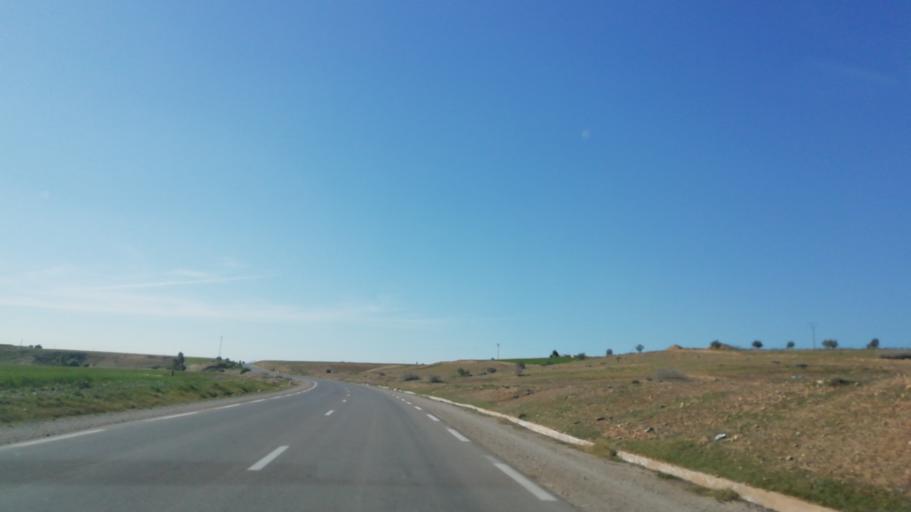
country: DZ
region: Mascara
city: Oued el Abtal
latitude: 35.4531
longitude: 0.7759
